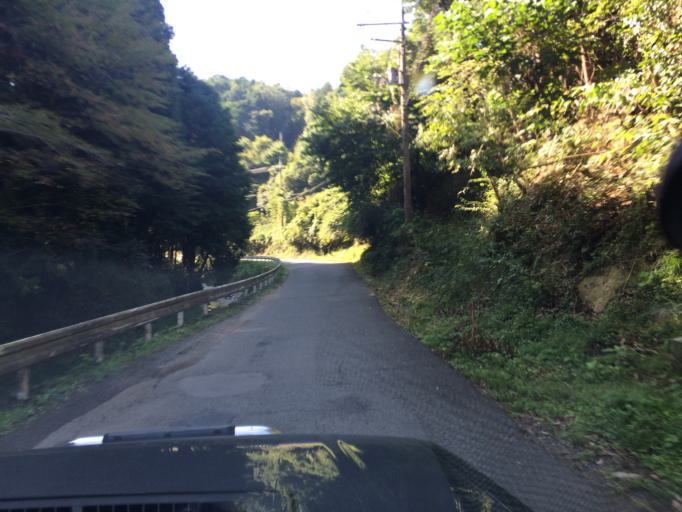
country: JP
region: Nara
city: Nara-shi
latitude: 34.7429
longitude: 135.9501
